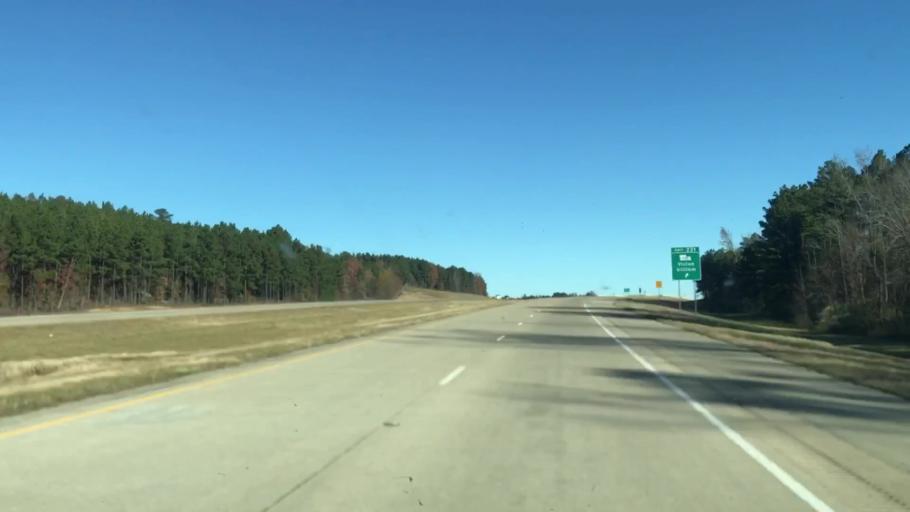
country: US
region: Louisiana
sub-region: Caddo Parish
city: Oil City
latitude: 32.8078
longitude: -93.8849
